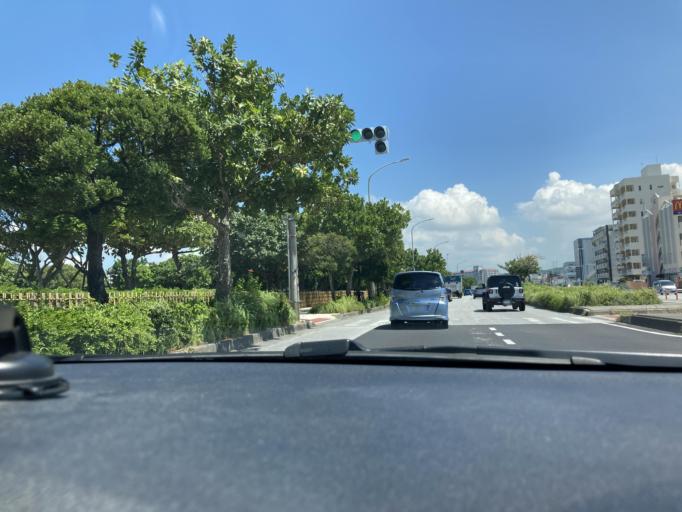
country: JP
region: Okinawa
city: Ginowan
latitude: 26.2787
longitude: 127.7341
